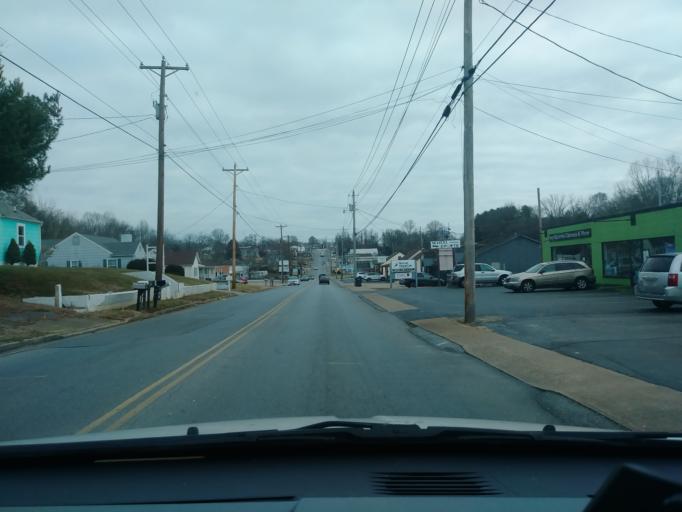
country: US
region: Tennessee
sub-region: Greene County
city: Greeneville
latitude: 36.1648
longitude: -82.8155
